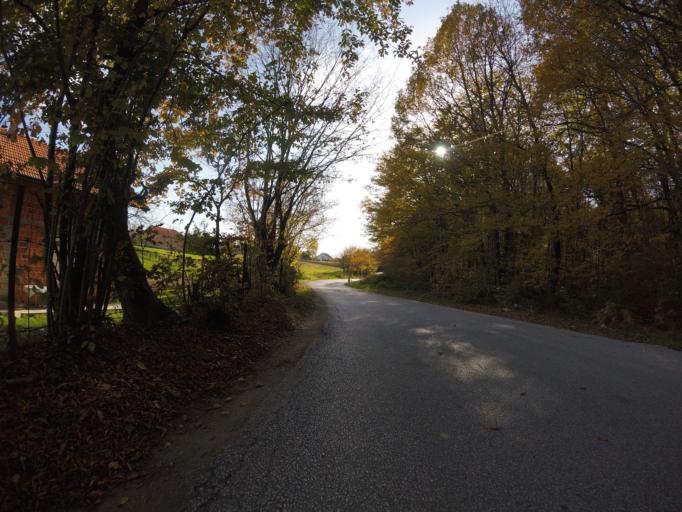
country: HR
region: Zagrebacka
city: Mraclin
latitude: 45.6097
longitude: 16.0671
